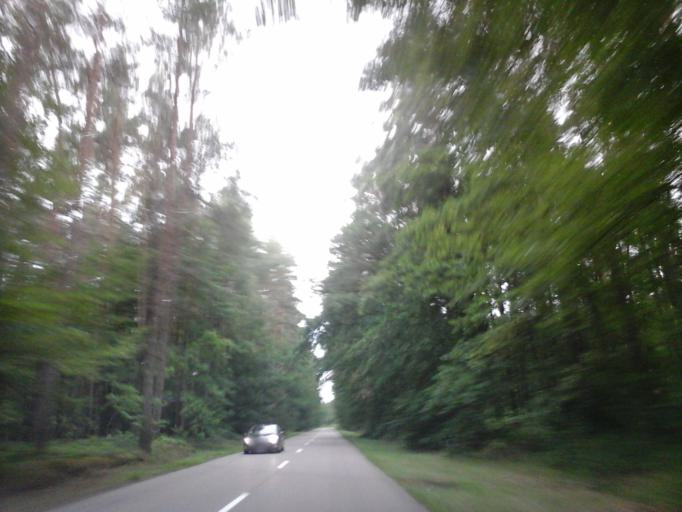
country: PL
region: West Pomeranian Voivodeship
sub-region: Powiat kamienski
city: Golczewo
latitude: 53.7705
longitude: 15.0240
